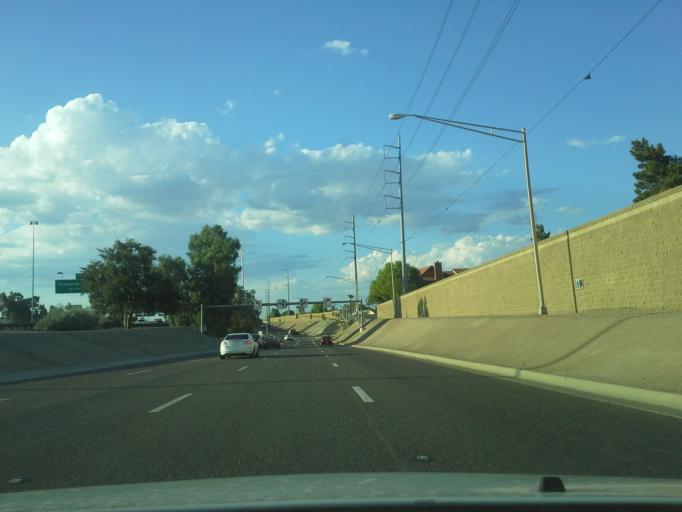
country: US
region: Arizona
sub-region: Maricopa County
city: Glendale
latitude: 33.5946
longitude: -112.1164
